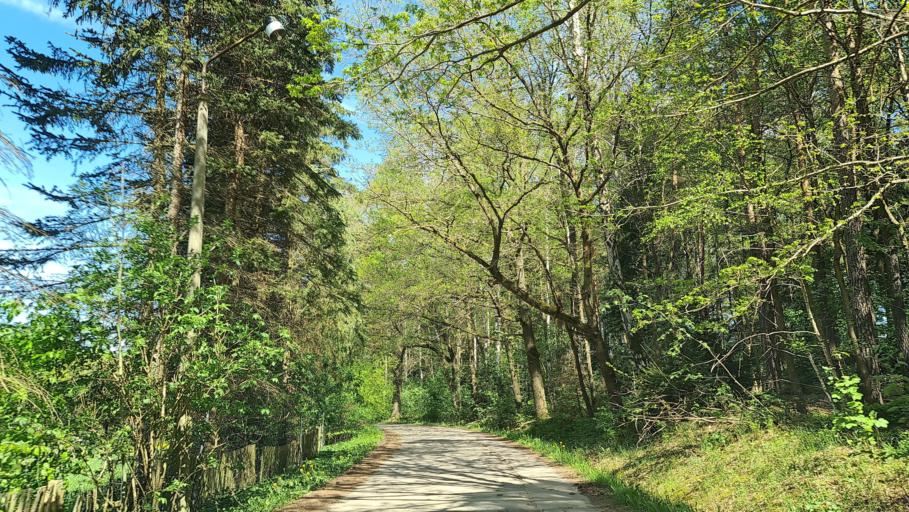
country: DE
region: Thuringia
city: Zeulenroda
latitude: 50.6439
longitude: 12.0113
